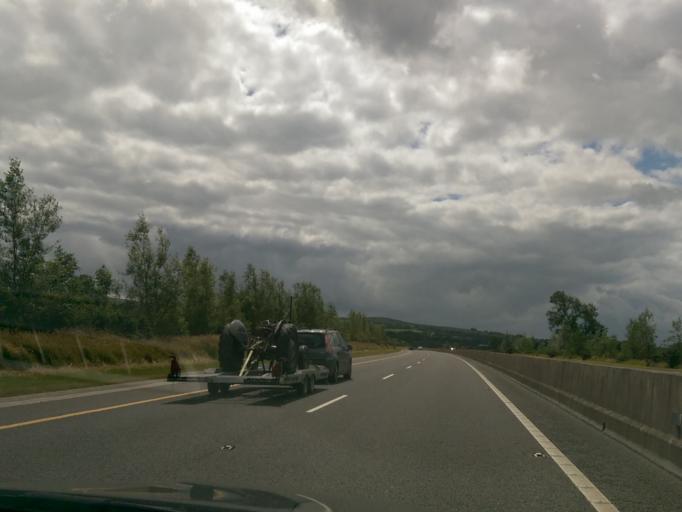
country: IE
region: Munster
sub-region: County Cork
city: Mitchelstown
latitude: 52.2647
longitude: -8.2474
